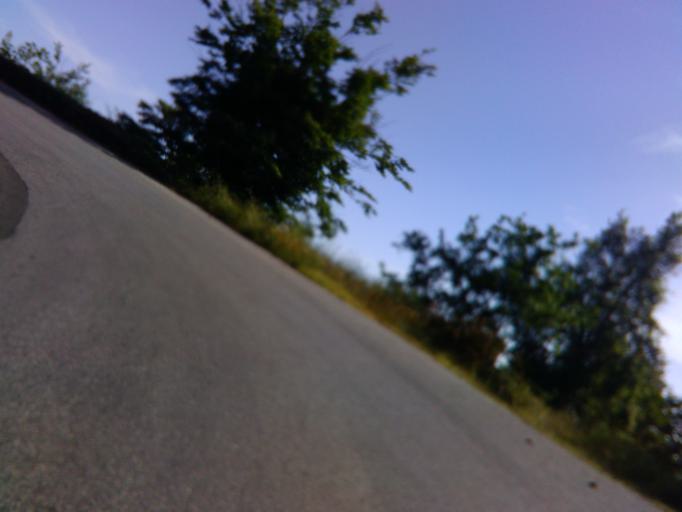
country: IT
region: Tuscany
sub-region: Provincia di Massa-Carrara
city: Fosdinovo
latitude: 44.1360
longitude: 10.0299
